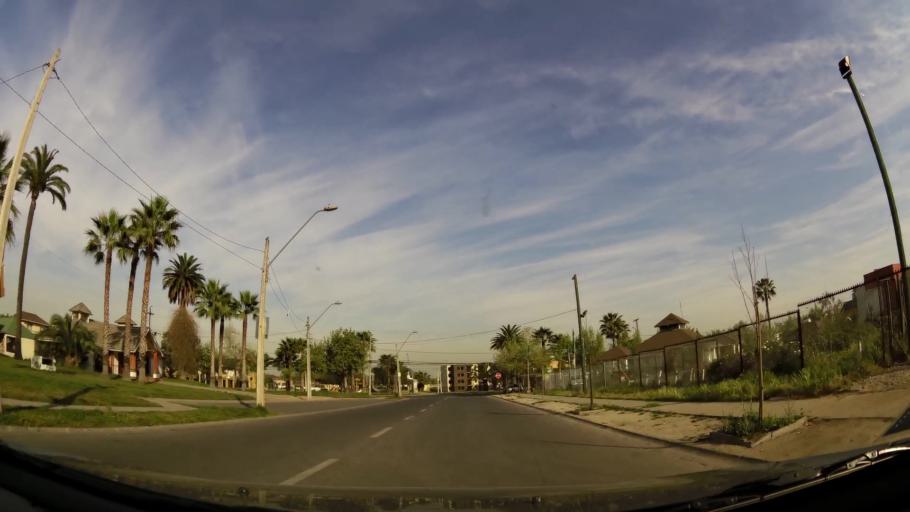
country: CL
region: Santiago Metropolitan
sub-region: Provincia de Cordillera
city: Puente Alto
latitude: -33.5617
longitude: -70.5493
